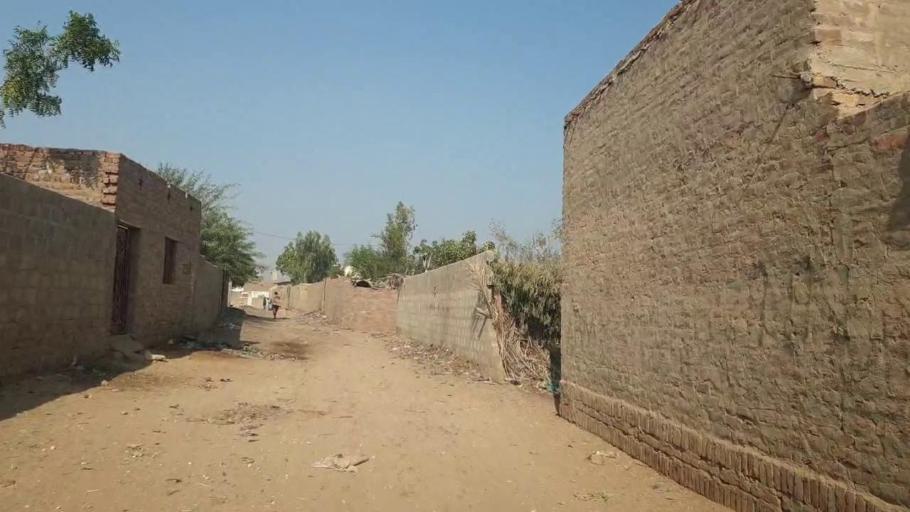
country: PK
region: Sindh
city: Jamshoro
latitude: 25.4390
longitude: 68.2814
